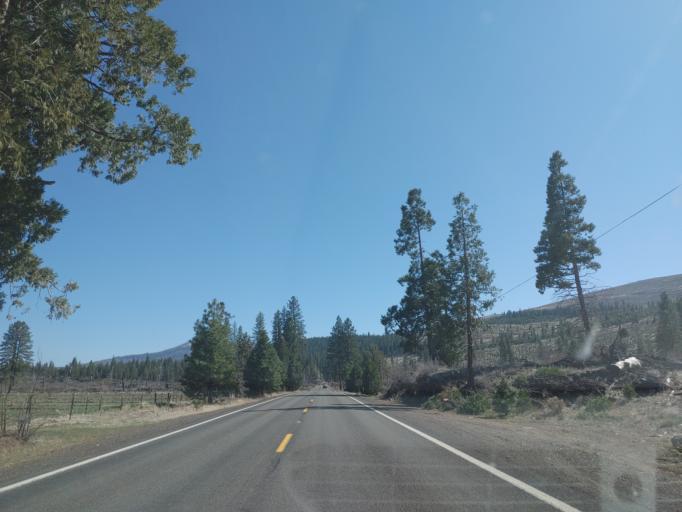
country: US
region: California
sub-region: Shasta County
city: Burney
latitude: 40.7683
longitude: -121.5007
